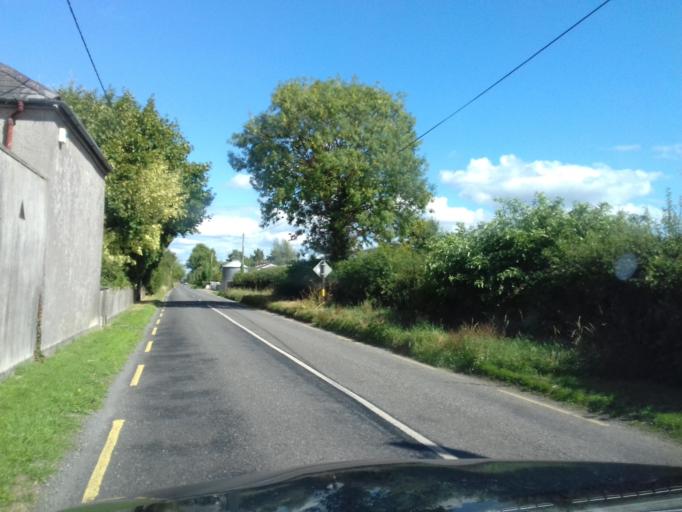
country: IE
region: Leinster
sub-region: Kilkenny
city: Callan
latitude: 52.5343
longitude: -7.3681
